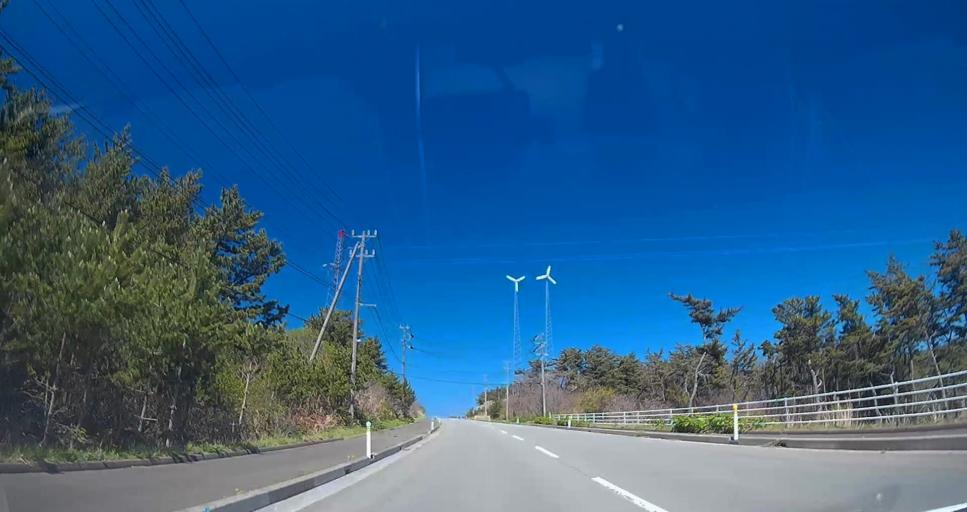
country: JP
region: Hokkaido
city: Hakodate
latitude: 41.5058
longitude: 140.9153
